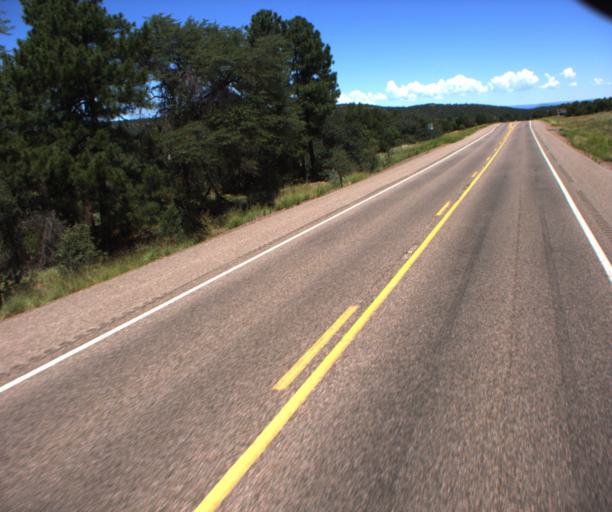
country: US
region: Arizona
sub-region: Gila County
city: San Carlos
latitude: 33.6707
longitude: -110.5725
